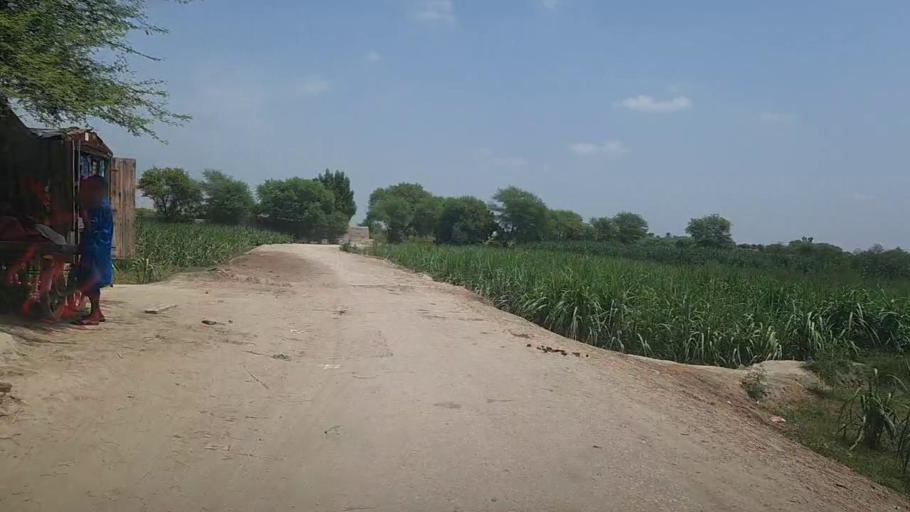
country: PK
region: Sindh
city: Ubauro
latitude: 28.2427
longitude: 69.8255
